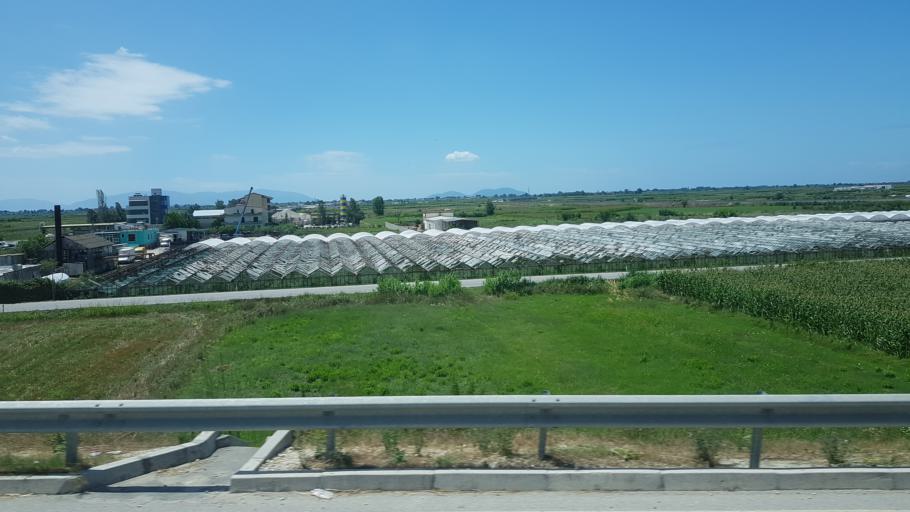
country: AL
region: Fier
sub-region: Rrethi i Fierit
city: Levan
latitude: 40.6700
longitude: 19.4838
